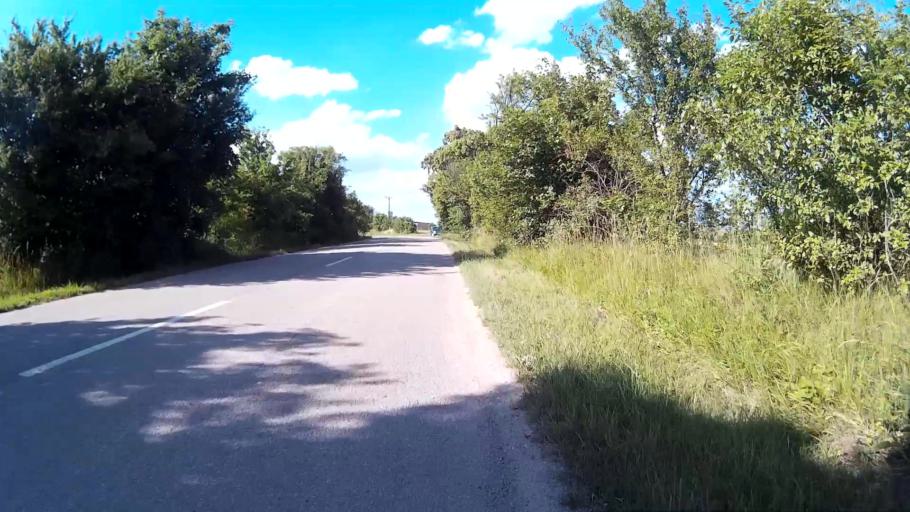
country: CZ
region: South Moravian
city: Sitborice
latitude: 49.0049
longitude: 16.7791
